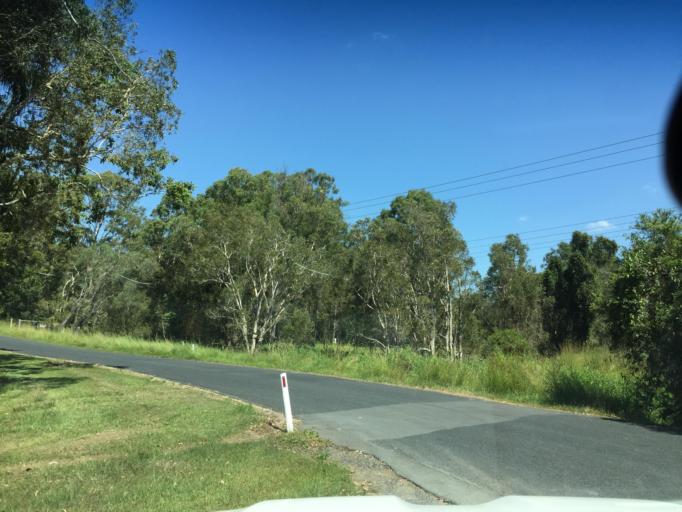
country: AU
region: Queensland
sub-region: Moreton Bay
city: Burpengary
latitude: -27.1784
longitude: 152.9746
